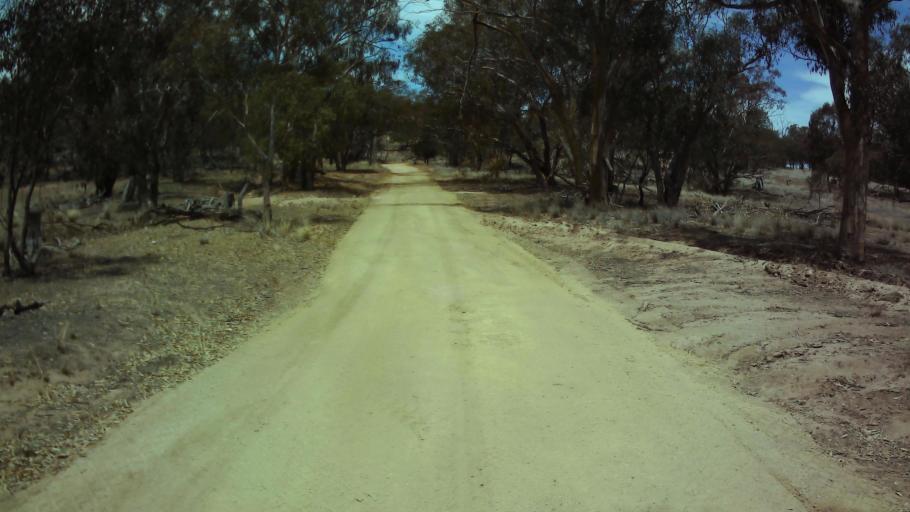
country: AU
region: New South Wales
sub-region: Weddin
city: Grenfell
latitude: -33.7861
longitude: 148.1541
